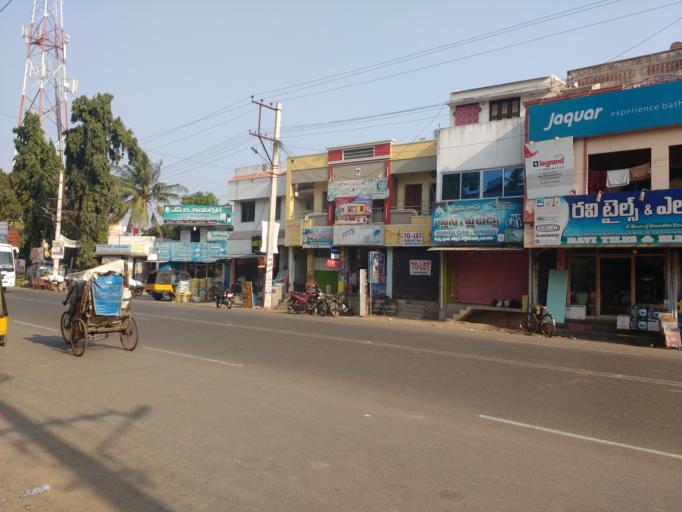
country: IN
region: Andhra Pradesh
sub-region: Srikakulam
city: Srikakulam
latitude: 18.2961
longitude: 83.9022
